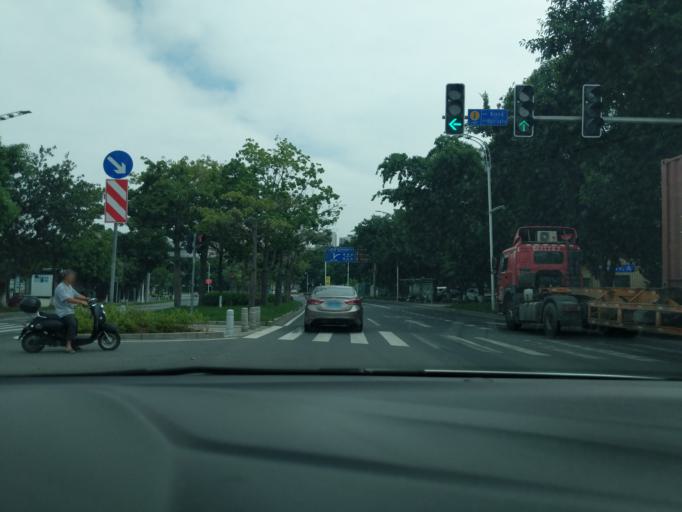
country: CN
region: Guangdong
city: Nansha
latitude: 22.7519
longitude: 113.5779
